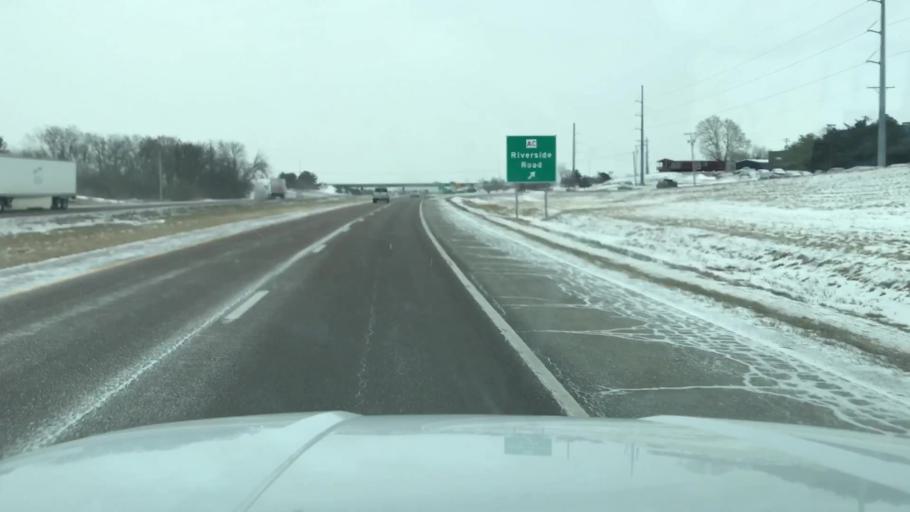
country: US
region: Missouri
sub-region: Buchanan County
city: Saint Joseph
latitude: 39.7510
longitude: -94.7743
